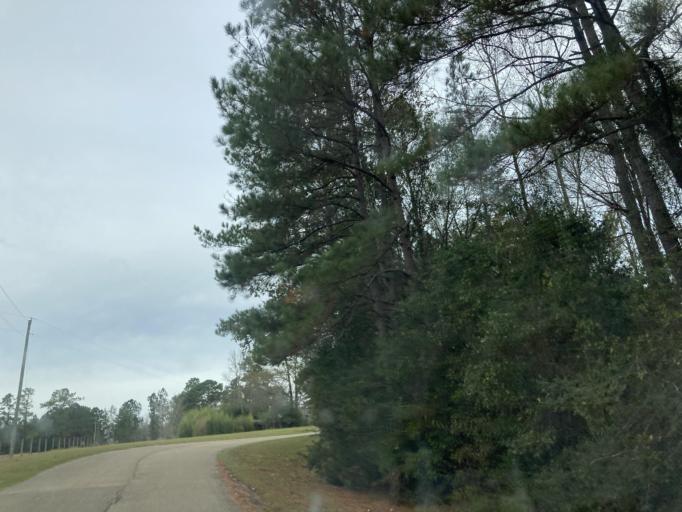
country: US
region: Mississippi
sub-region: Lamar County
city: Purvis
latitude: 31.1183
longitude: -89.4546
